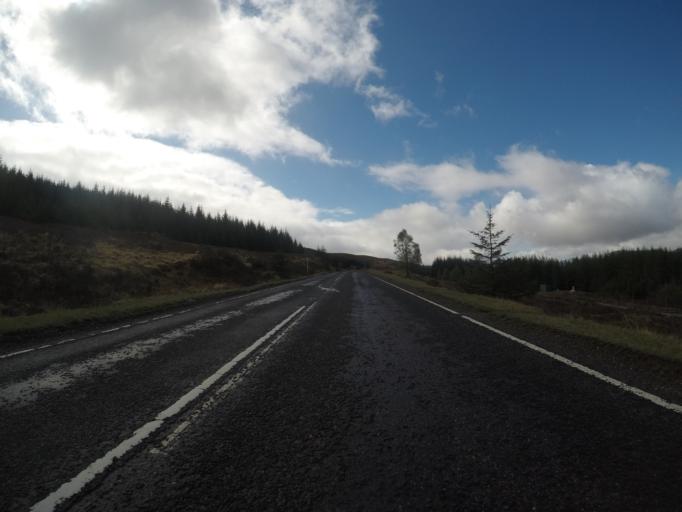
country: GB
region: Scotland
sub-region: Highland
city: Spean Bridge
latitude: 57.1095
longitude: -4.9844
